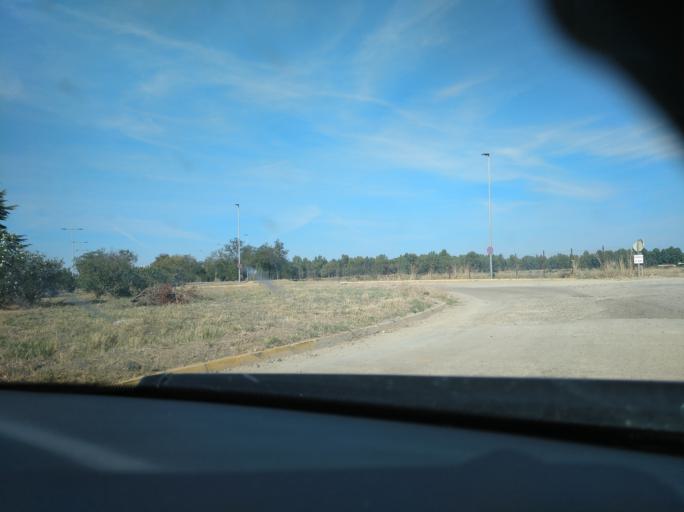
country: ES
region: Extremadura
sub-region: Provincia de Badajoz
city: Badajoz
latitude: 38.8776
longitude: -7.0258
